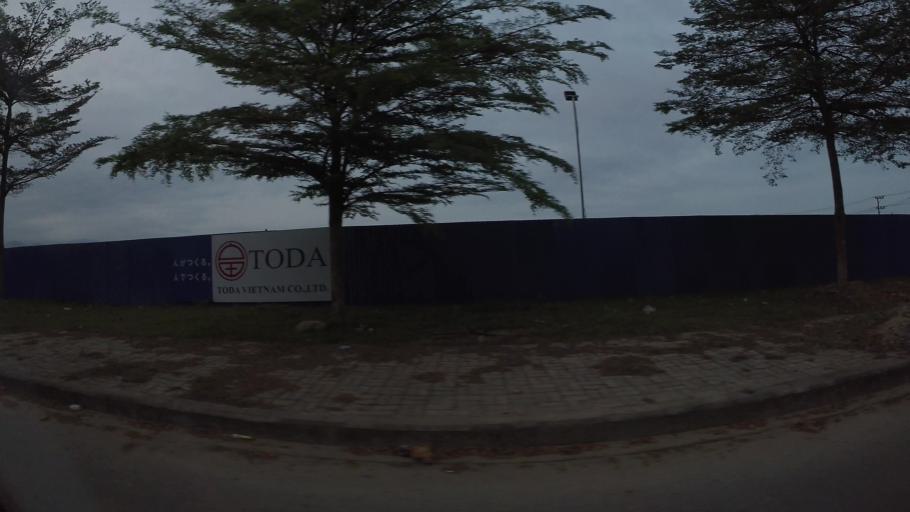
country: VN
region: Da Nang
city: Lien Chieu
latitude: 16.0884
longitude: 108.1109
